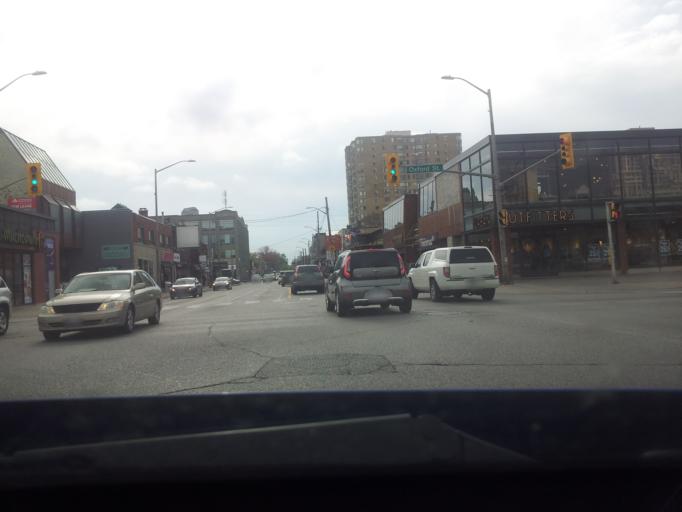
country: CA
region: Ontario
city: London
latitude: 42.9954
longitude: -81.2534
